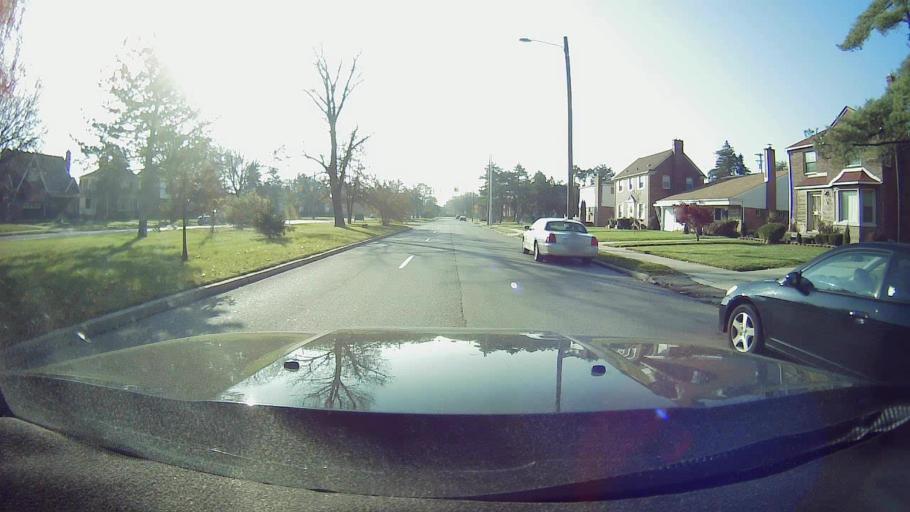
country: US
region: Michigan
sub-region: Wayne County
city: Highland Park
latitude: 42.3817
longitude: -83.1441
